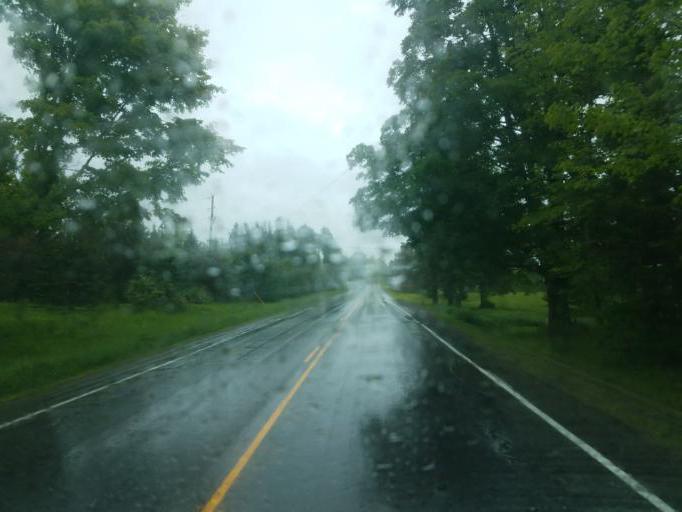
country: US
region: New York
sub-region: Herkimer County
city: Ilion
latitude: 42.9337
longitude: -75.0497
